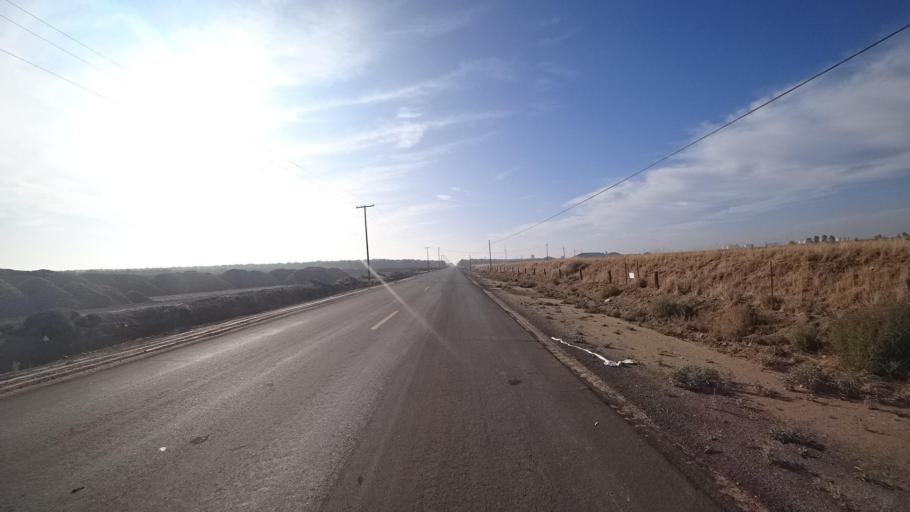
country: US
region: California
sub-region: Kern County
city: McFarland
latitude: 35.6413
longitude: -119.2045
